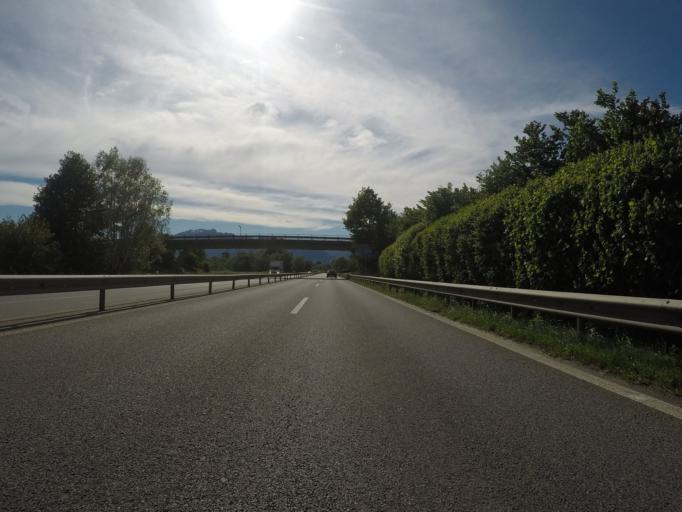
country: CH
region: Ticino
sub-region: Locarno District
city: Gordola
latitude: 46.1683
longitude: 8.8804
